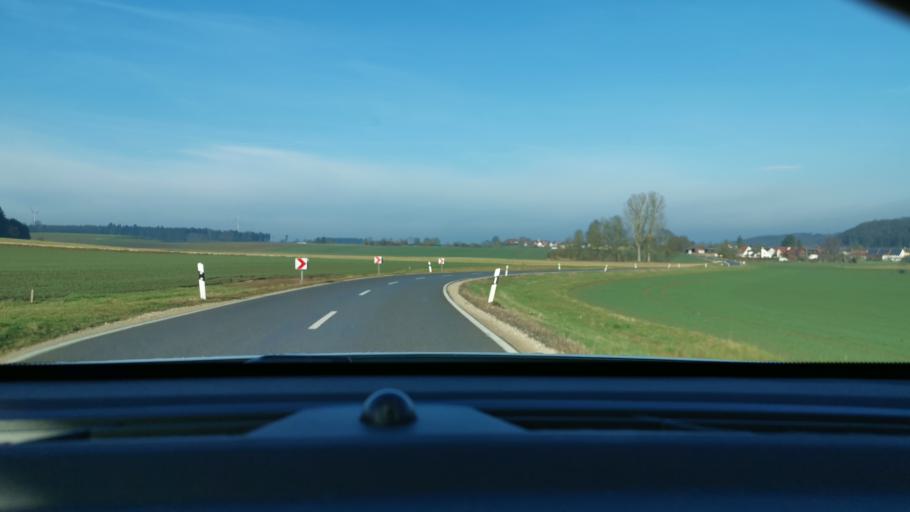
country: DE
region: Bavaria
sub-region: Swabia
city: Holzheim
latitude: 48.5775
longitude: 10.9661
